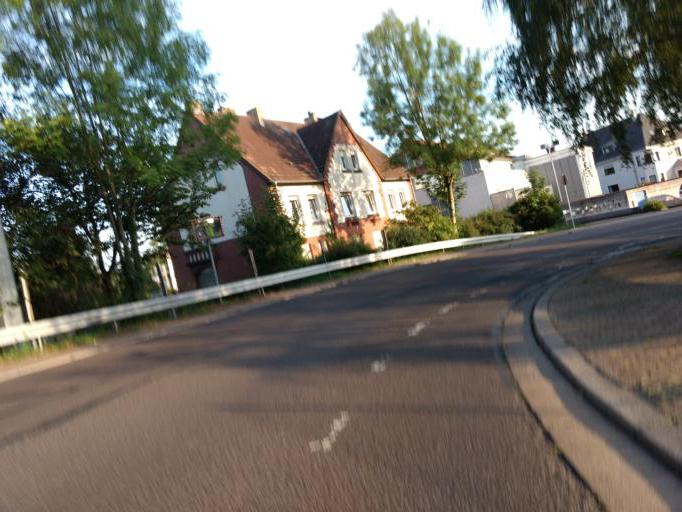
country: DE
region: Saarland
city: Dillingen
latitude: 49.3486
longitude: 6.7269
